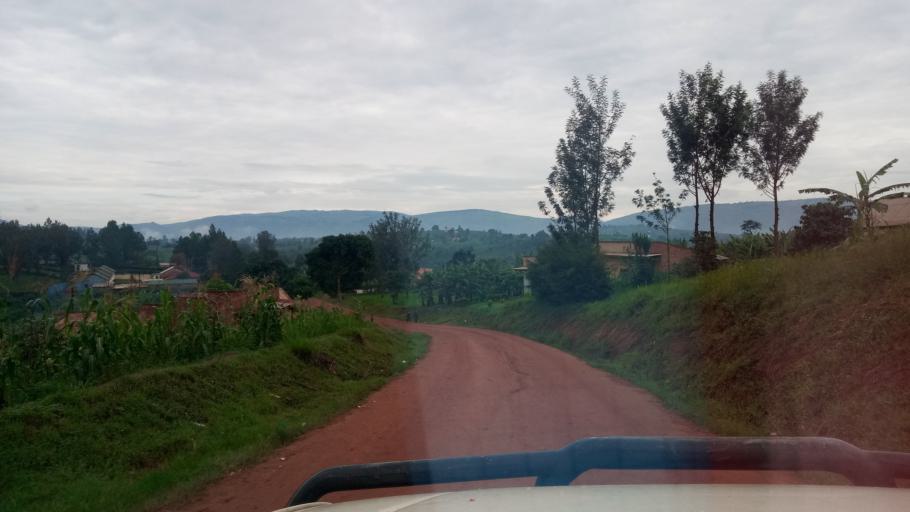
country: UG
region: Western Region
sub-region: Buhweju District
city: Buhweju
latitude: -0.1692
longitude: 30.4639
